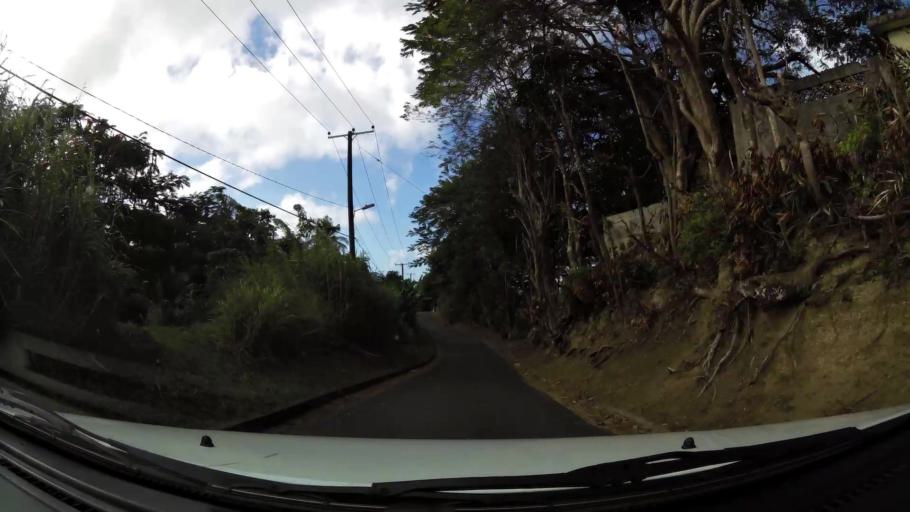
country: LC
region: Castries Quarter
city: Bisee
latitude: 14.0101
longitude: -60.9716
